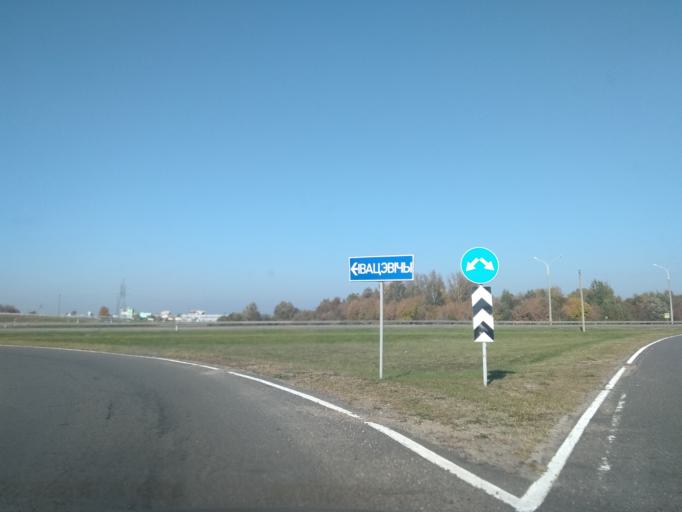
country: BY
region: Brest
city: Ivatsevichy
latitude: 52.6996
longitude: 25.3653
